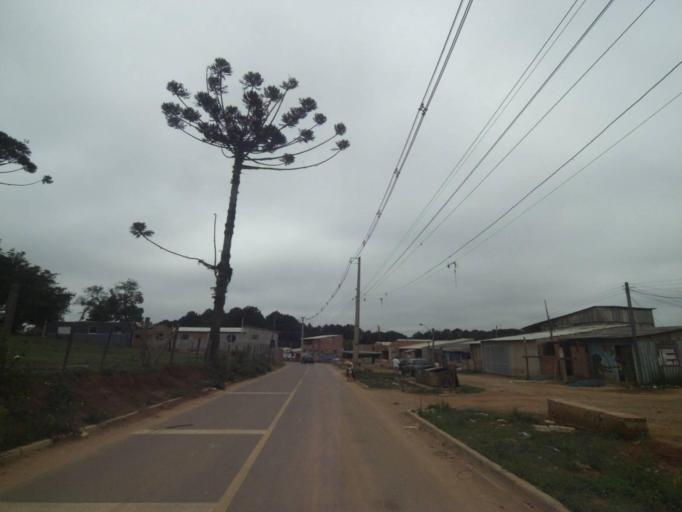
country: BR
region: Parana
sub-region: Araucaria
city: Araucaria
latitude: -25.5090
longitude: -49.3525
